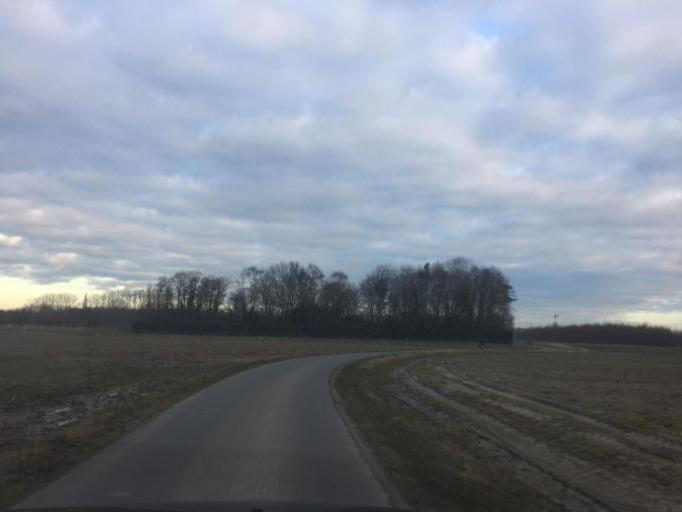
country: BE
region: Flanders
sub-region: Provincie West-Vlaanderen
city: Roeselare
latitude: 50.9890
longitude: 3.1323
